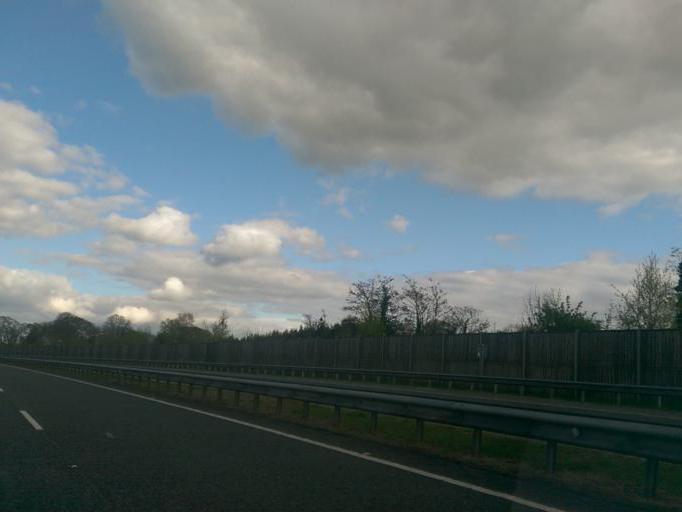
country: IE
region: Leinster
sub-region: An Iarmhi
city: Athlone
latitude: 53.4025
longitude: -7.8685
